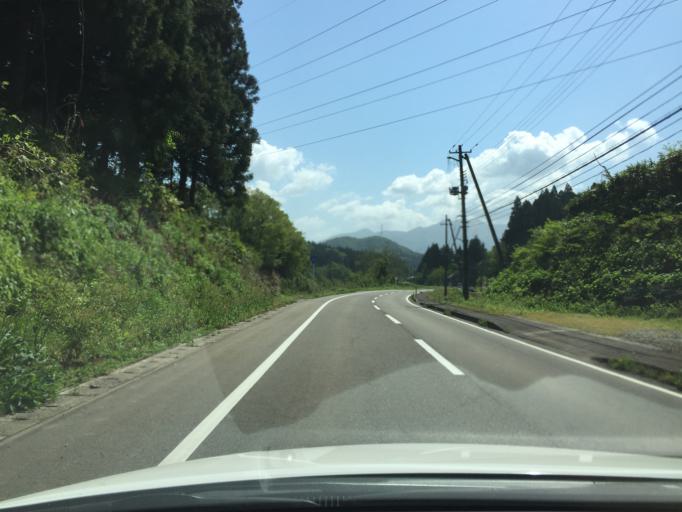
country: JP
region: Niigata
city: Kamo
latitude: 37.5771
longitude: 139.0764
